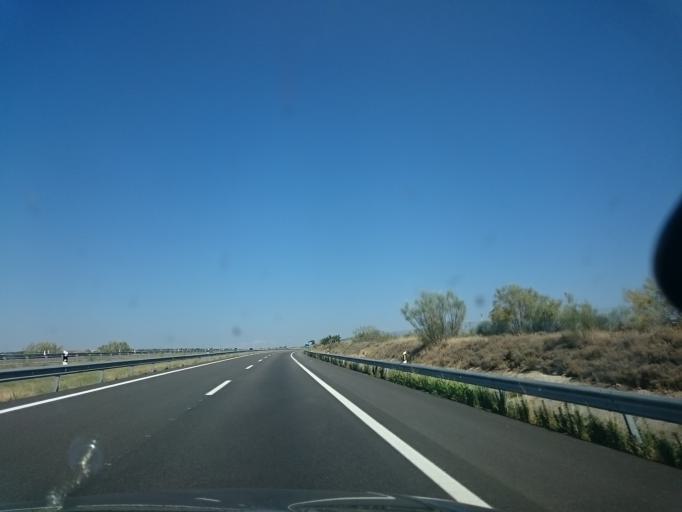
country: ES
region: Aragon
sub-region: Provincia de Zaragoza
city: Mequinensa / Mequinenza
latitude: 41.4689
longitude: 0.2572
